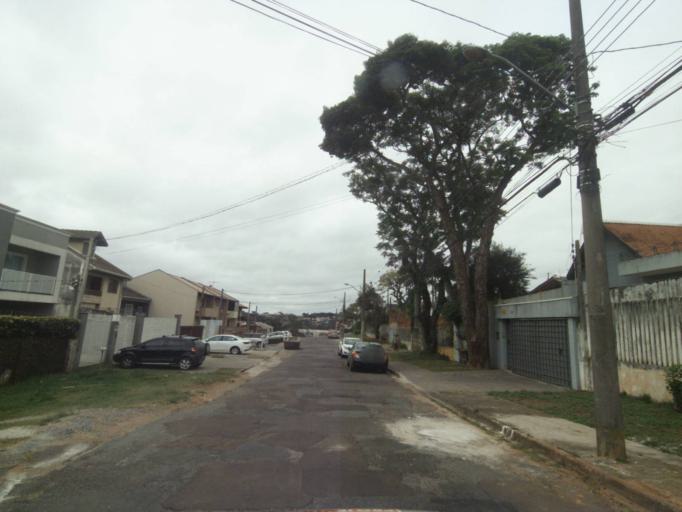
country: BR
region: Parana
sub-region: Sao Jose Dos Pinhais
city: Sao Jose dos Pinhais
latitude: -25.4847
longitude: -49.2286
